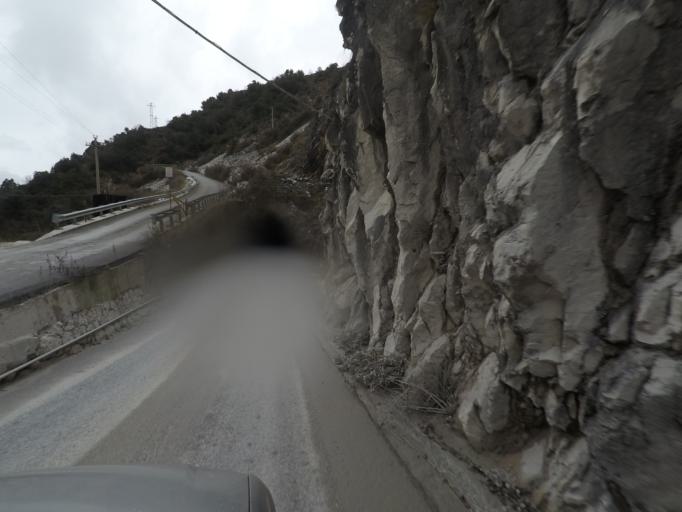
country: IT
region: Tuscany
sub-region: Provincia di Massa-Carrara
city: Massa
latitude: 44.0808
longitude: 10.1329
